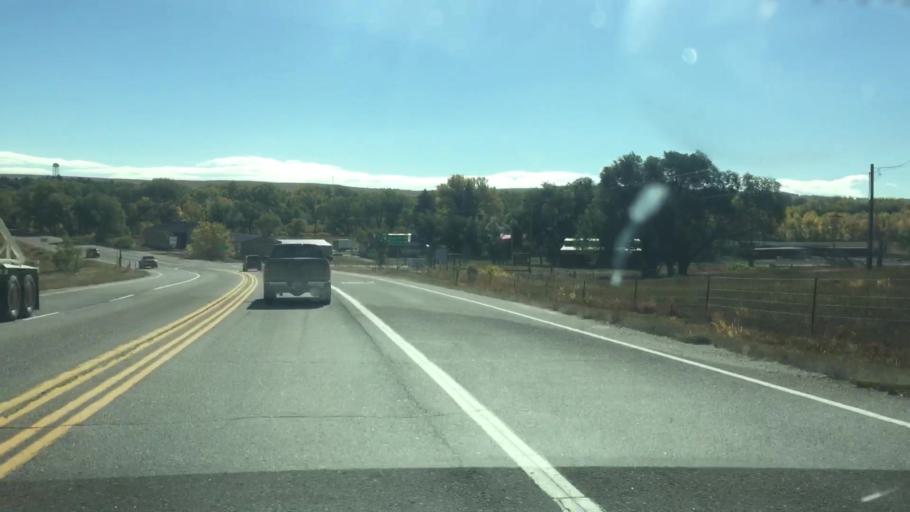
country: US
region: Colorado
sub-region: Elbert County
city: Kiowa
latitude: 39.3471
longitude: -104.4751
